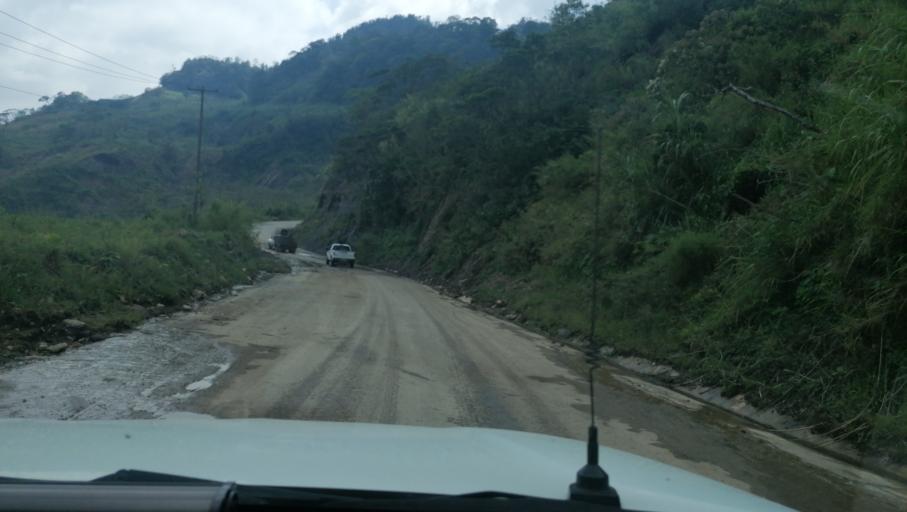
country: MX
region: Chiapas
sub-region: Ocotepec
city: San Pablo Huacano
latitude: 17.2629
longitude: -93.2669
